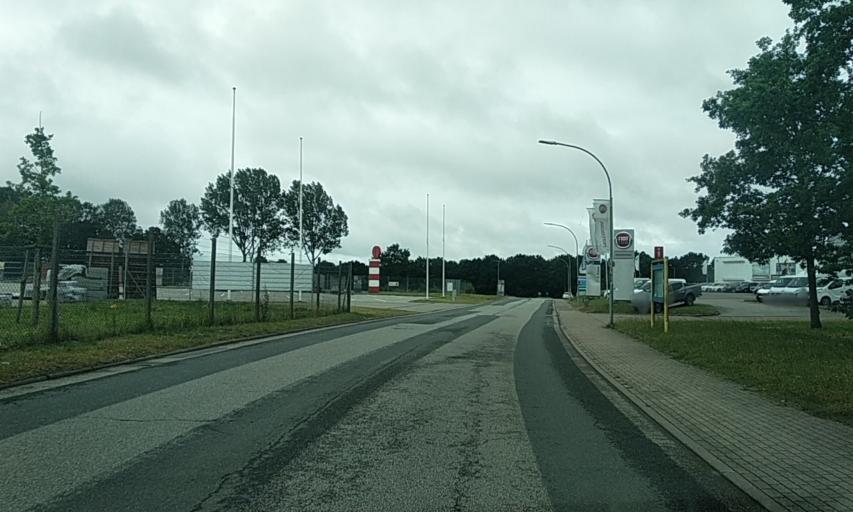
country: DE
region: Schleswig-Holstein
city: Schleswig
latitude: 54.5318
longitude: 9.5837
